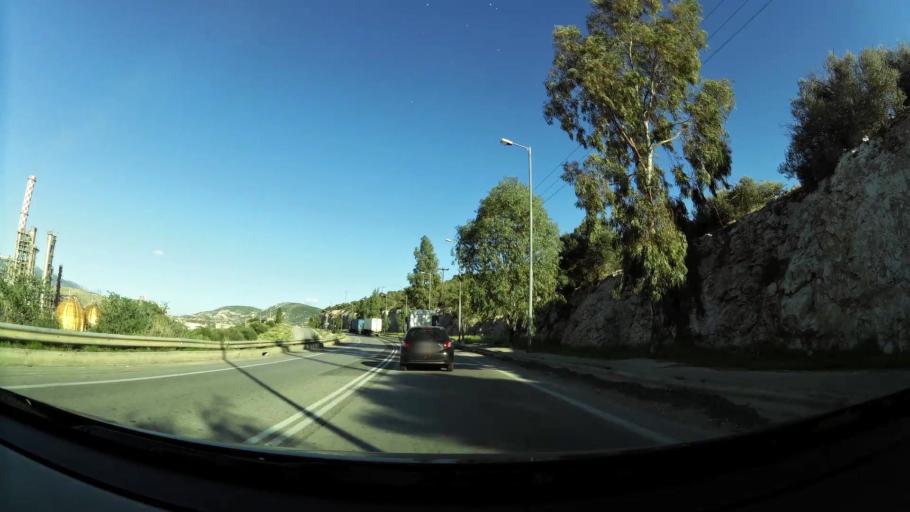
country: GR
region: Attica
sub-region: Nomarchia Athinas
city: Skaramangas
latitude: 38.0276
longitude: 23.6038
